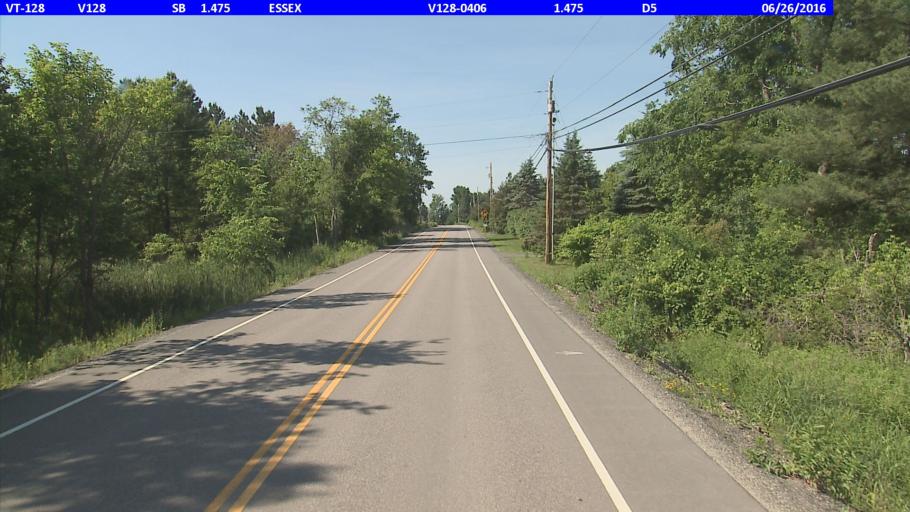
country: US
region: Vermont
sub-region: Chittenden County
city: Jericho
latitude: 44.5194
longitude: -73.0344
